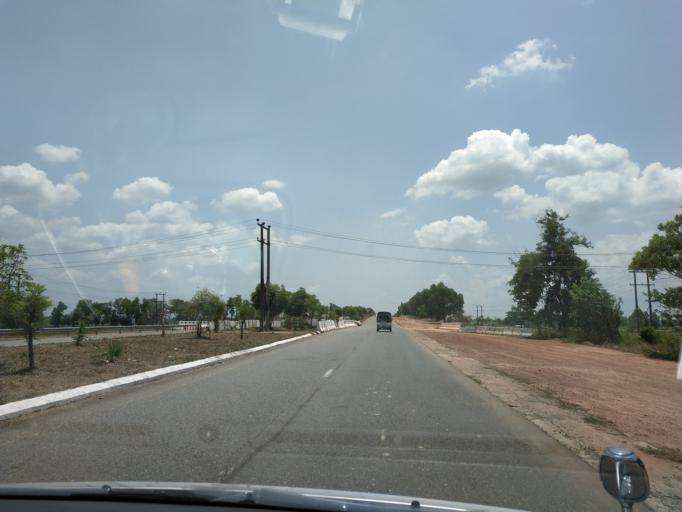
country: MM
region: Bago
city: Thanatpin
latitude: 17.2237
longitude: 96.2088
